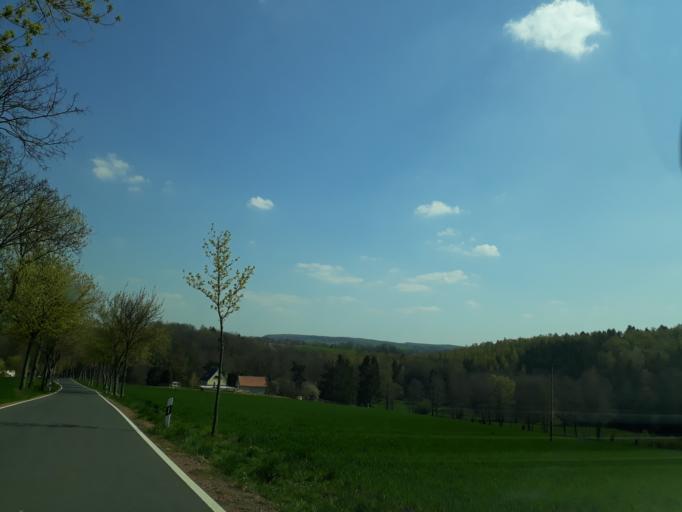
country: DE
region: Saxony
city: Niederschona
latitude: 51.0270
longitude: 13.4585
